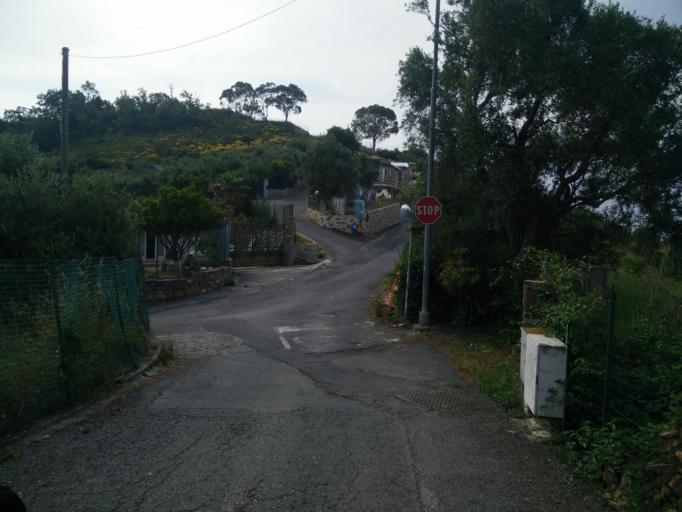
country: IT
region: Liguria
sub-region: Provincia di Imperia
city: Imperia
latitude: 43.8761
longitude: 8.0004
